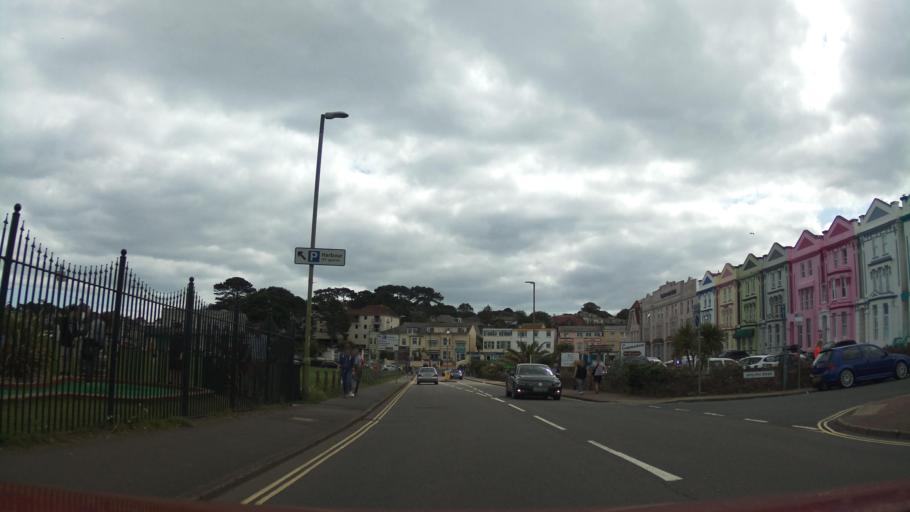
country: GB
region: England
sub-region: Borough of Torbay
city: Paignton
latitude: 50.4343
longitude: -3.5601
